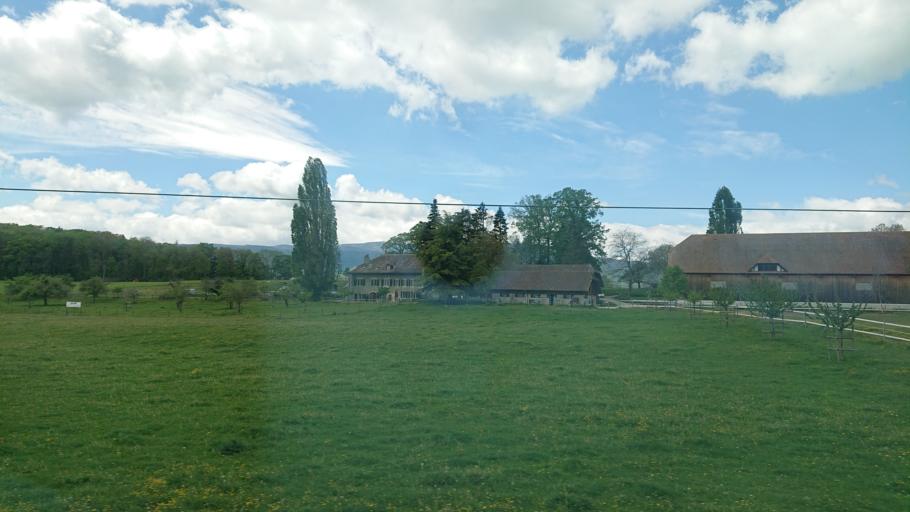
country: CH
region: Vaud
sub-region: Nyon District
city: Nyon
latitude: 46.3757
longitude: 6.2259
